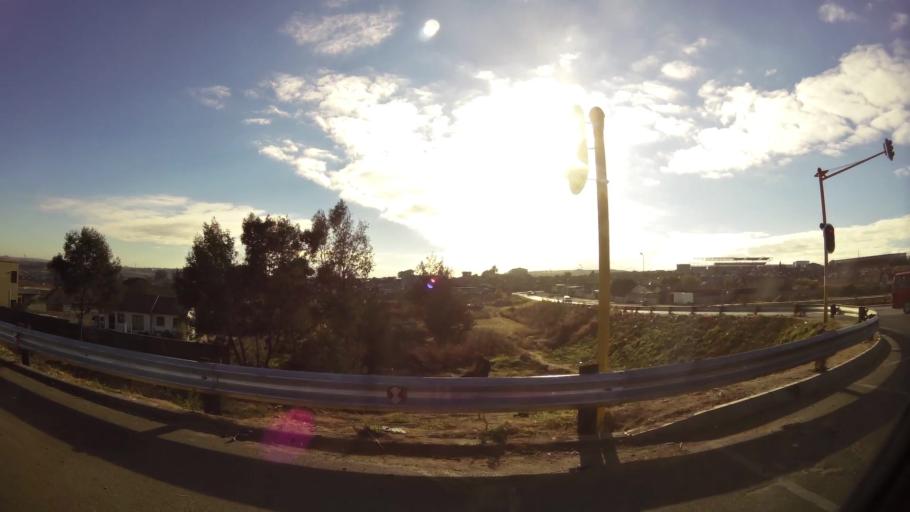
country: ZA
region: Gauteng
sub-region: City of Johannesburg Metropolitan Municipality
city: Modderfontein
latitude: -26.0502
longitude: 28.1580
